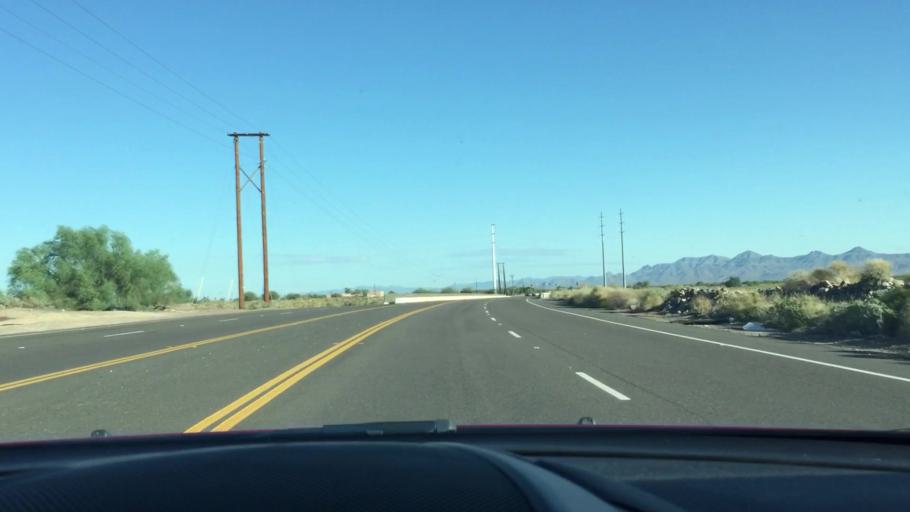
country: US
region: Arizona
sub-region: Maricopa County
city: Mesa
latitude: 33.4511
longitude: -111.8572
